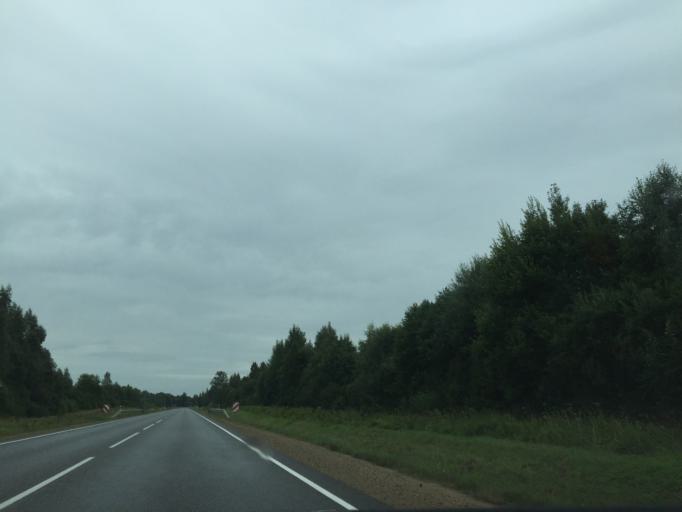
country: LV
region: Livani
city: Livani
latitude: 56.3950
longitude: 26.1431
